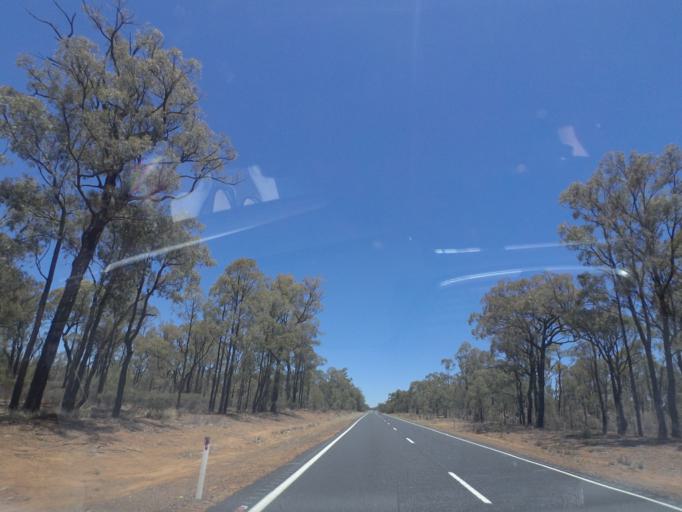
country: AU
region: New South Wales
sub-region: Warrumbungle Shire
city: Coonabarabran
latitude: -30.8625
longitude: 149.4535
